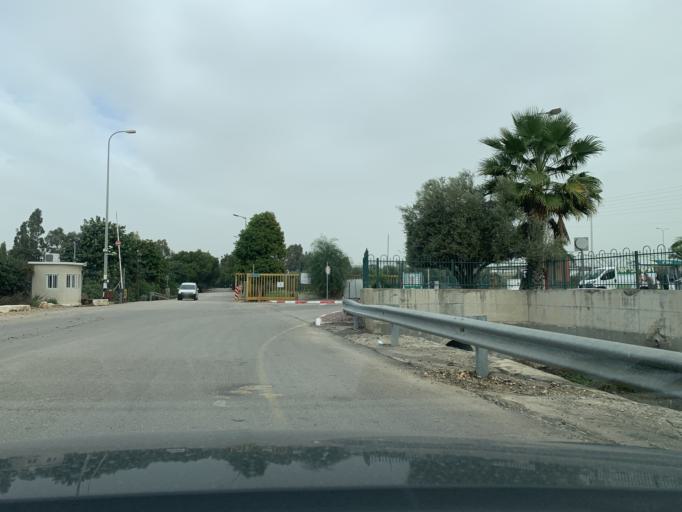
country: IL
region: Central District
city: Jaljulya
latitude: 32.1554
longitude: 34.9466
